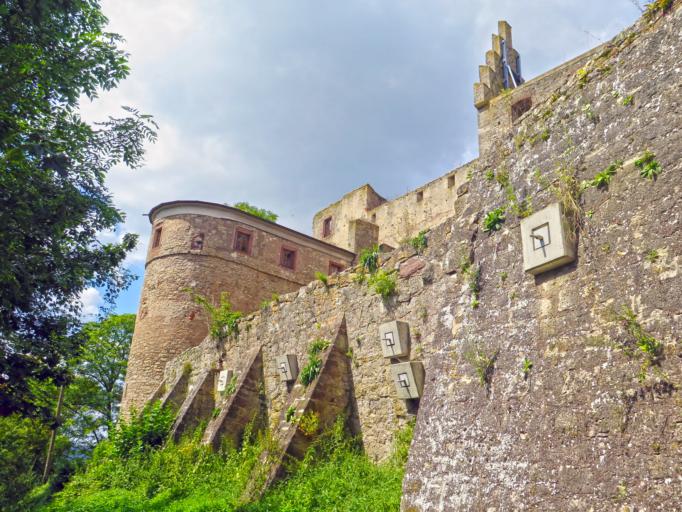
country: DE
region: Bavaria
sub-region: Regierungsbezirk Unterfranken
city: Elfershausen
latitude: 50.1354
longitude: 9.9818
